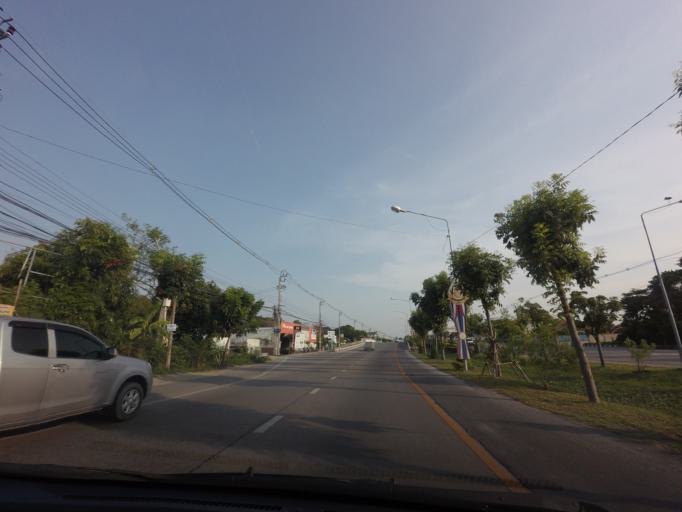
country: TH
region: Bangkok
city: Taling Chan
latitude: 13.7637
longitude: 100.4269
